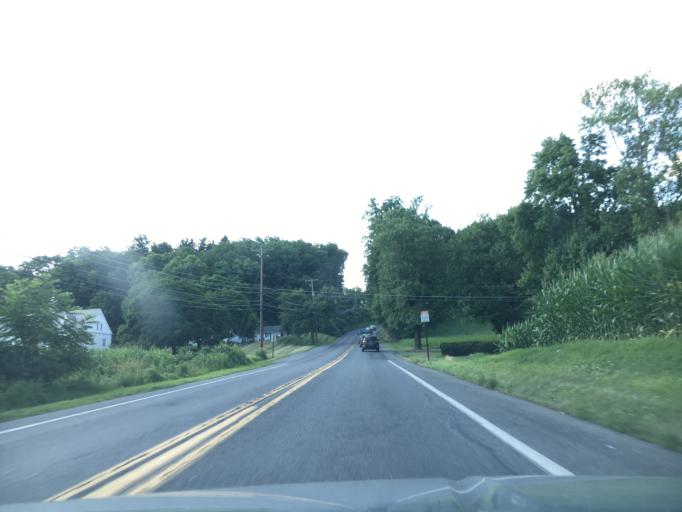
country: US
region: Pennsylvania
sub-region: Lehigh County
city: Dorneyville
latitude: 40.6170
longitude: -75.5348
